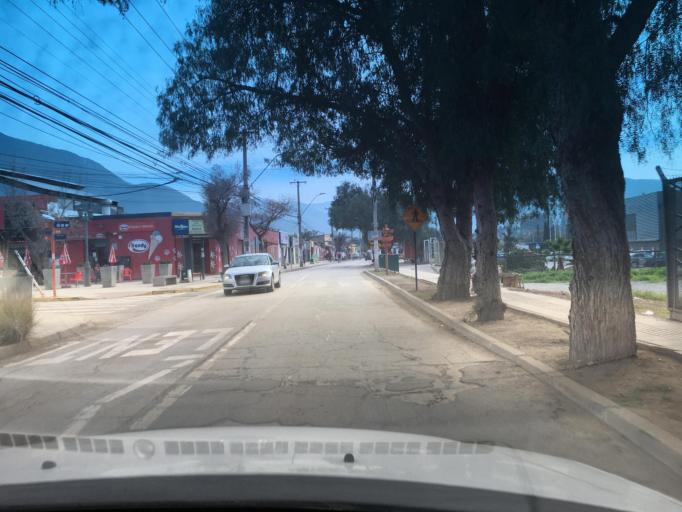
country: CL
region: Santiago Metropolitan
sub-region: Provincia de Chacabuco
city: Lampa
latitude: -33.0853
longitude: -70.9290
